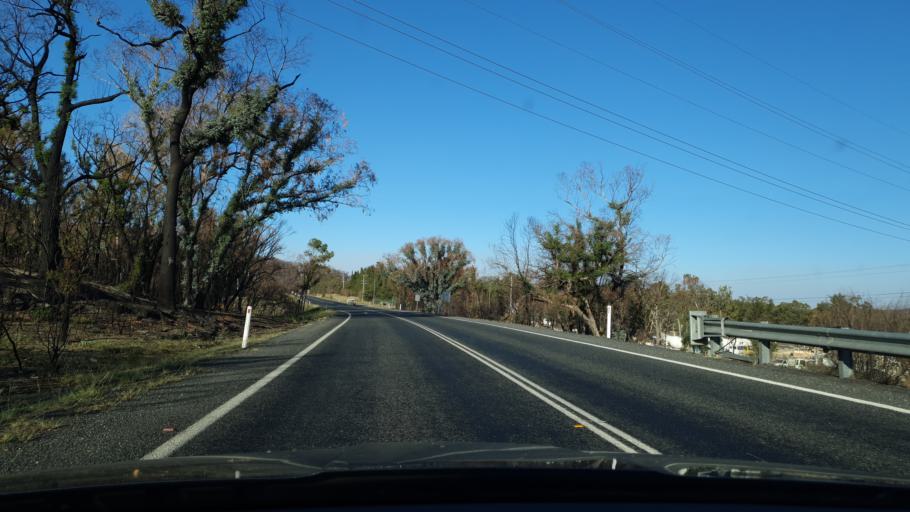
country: AU
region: Queensland
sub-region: Southern Downs
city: Stanthorpe
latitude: -28.6504
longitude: 151.9217
